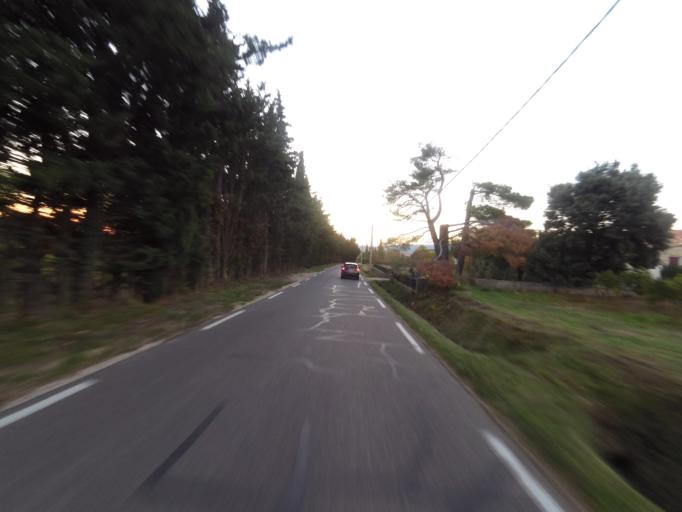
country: FR
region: Provence-Alpes-Cote d'Azur
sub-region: Departement du Vaucluse
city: Bedoin
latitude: 44.1211
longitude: 5.1933
